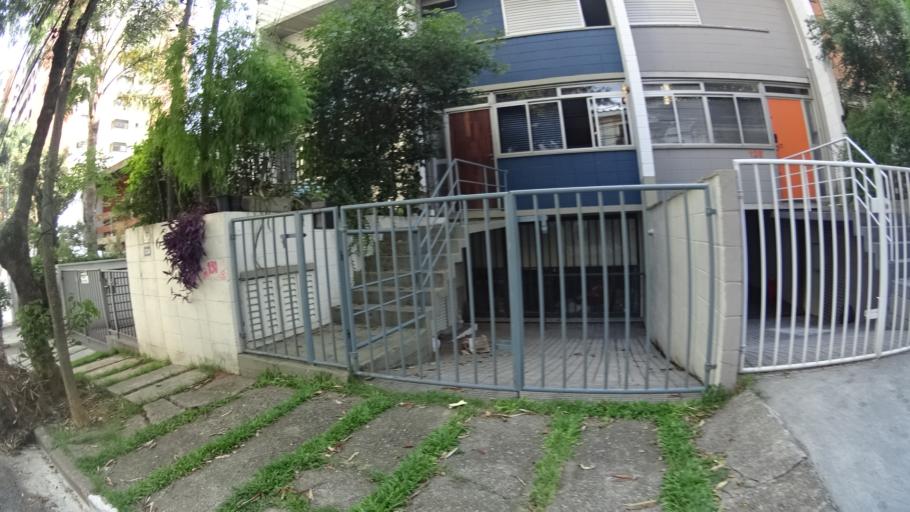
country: BR
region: Sao Paulo
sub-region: Sao Paulo
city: Sao Paulo
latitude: -23.5908
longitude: -46.6283
